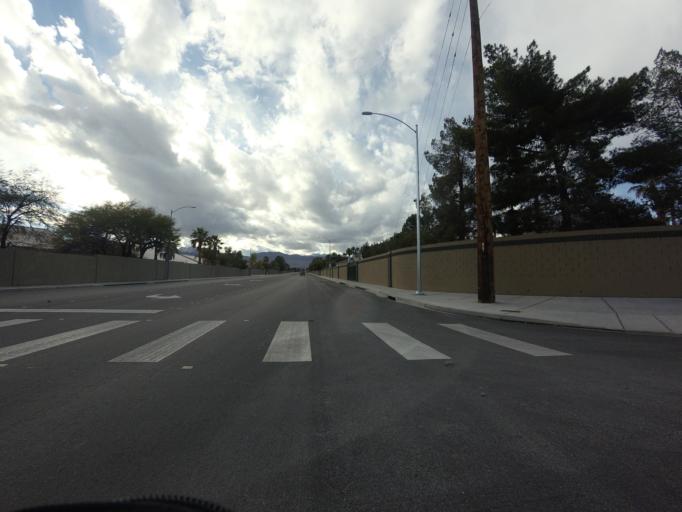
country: US
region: Nevada
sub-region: Clark County
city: Las Vegas
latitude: 36.2697
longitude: -115.2426
